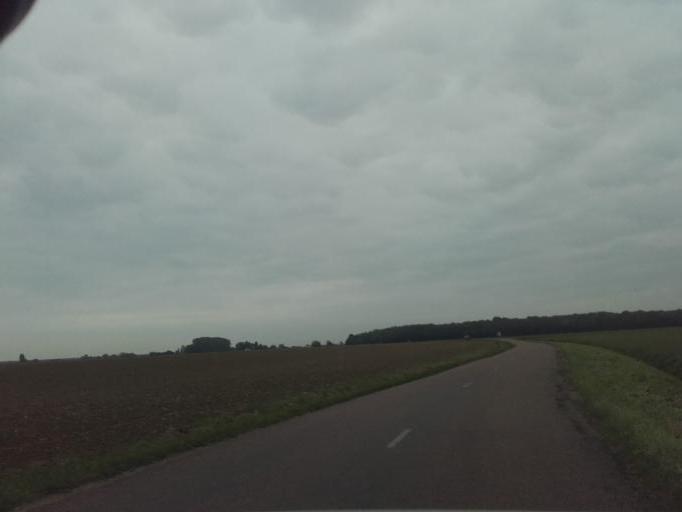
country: FR
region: Bourgogne
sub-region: Departement de la Cote-d'Or
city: Bligny-les-Beaune
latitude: 46.9729
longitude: 4.8646
